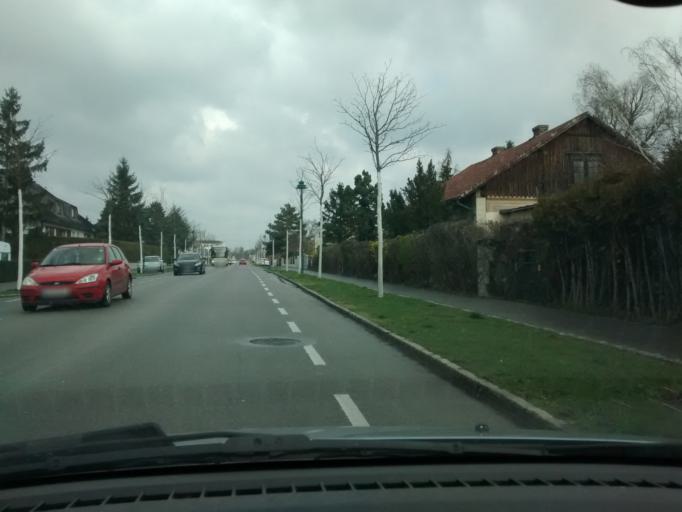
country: AT
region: Lower Austria
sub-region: Politischer Bezirk Modling
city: Laxenburg
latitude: 48.0731
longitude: 16.3541
